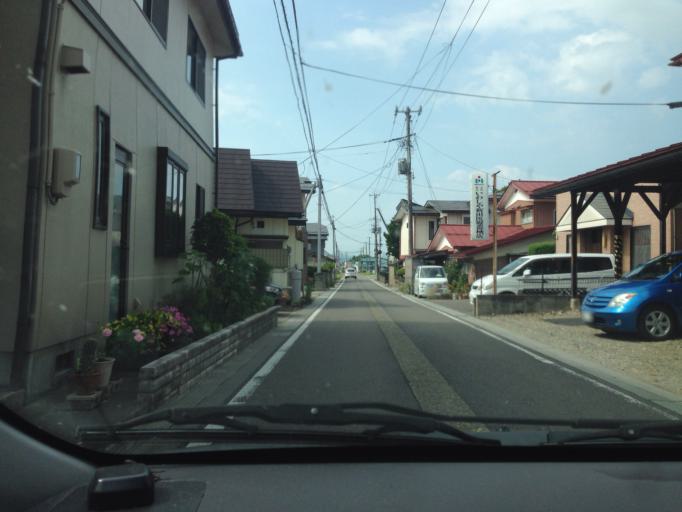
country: JP
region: Fukushima
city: Kitakata
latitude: 37.6514
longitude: 139.8659
